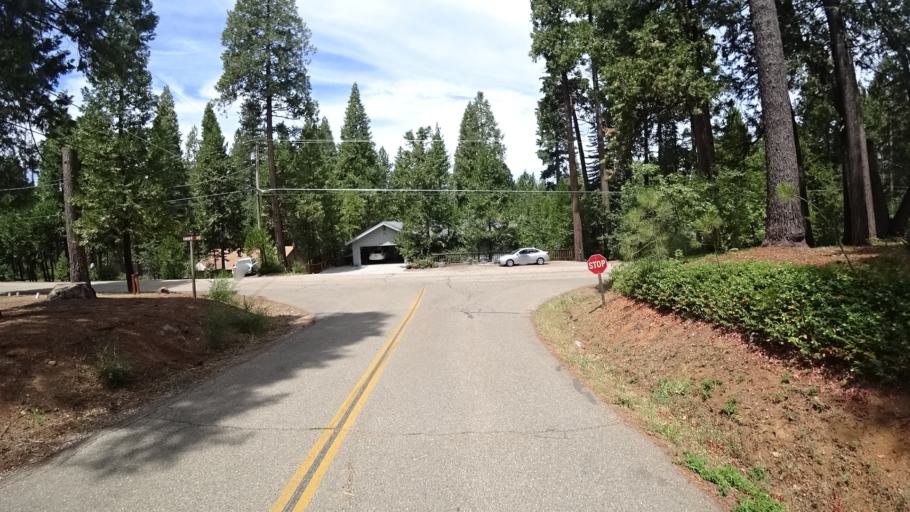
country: US
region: California
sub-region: Calaveras County
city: Arnold
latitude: 38.2376
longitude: -120.3603
